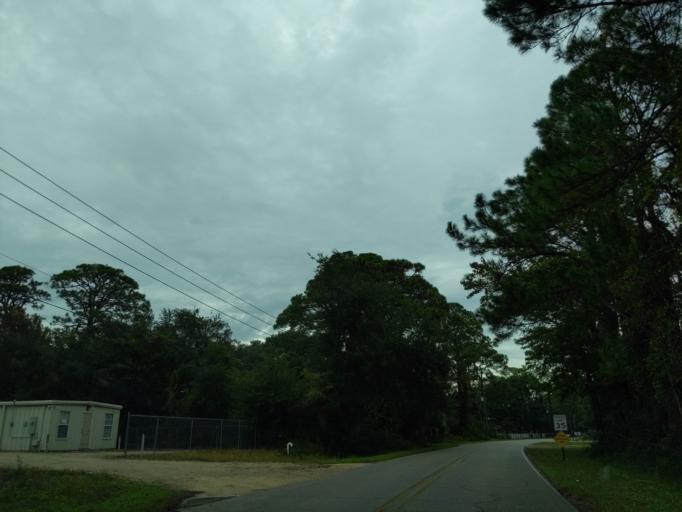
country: US
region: Florida
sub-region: Franklin County
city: Eastpoint
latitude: 29.7317
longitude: -84.8866
